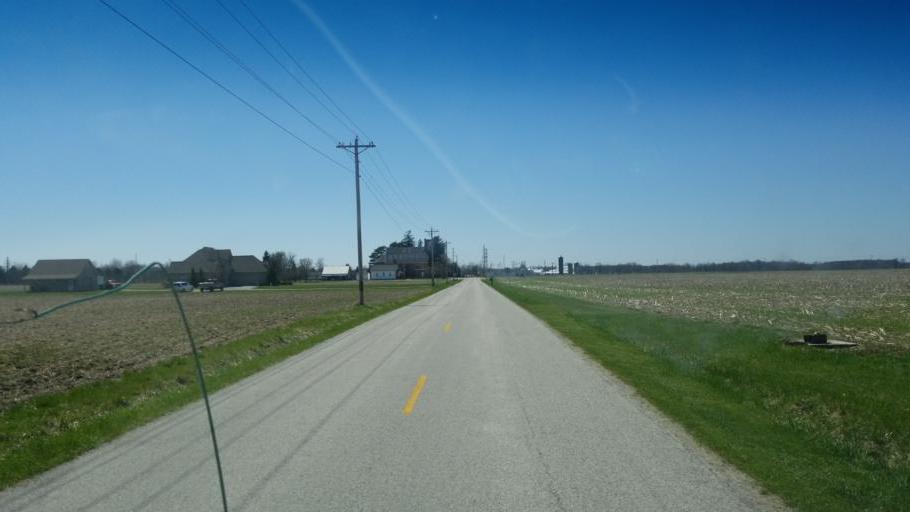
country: US
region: Ohio
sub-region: Crawford County
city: Bucyrus
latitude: 41.0229
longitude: -82.9521
